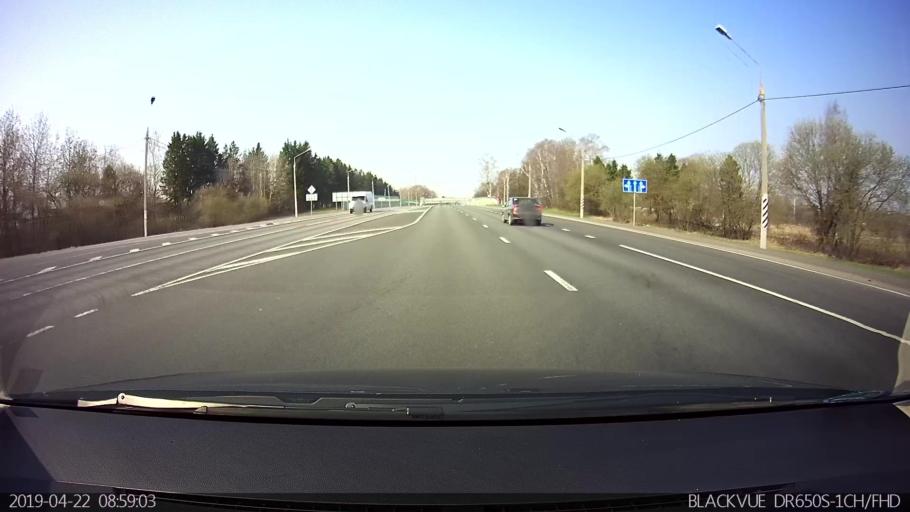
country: RU
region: Smolensk
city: Pechersk
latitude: 54.8640
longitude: 31.9785
